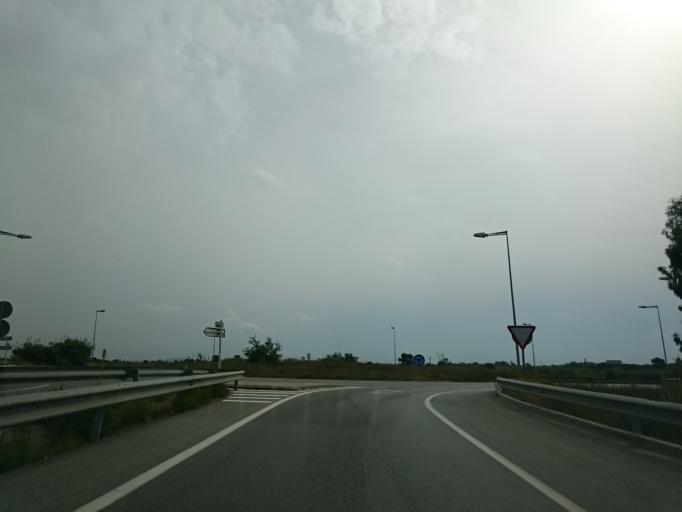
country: ES
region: Catalonia
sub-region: Provincia de Barcelona
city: Viladecans
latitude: 41.2781
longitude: 2.0519
